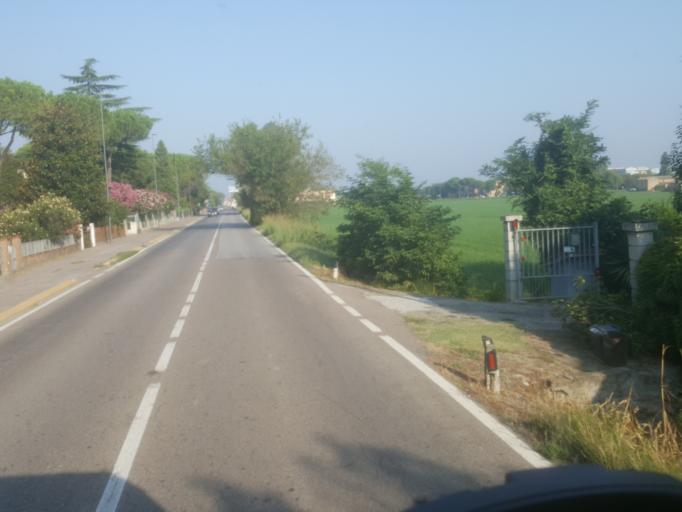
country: IT
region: Emilia-Romagna
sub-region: Provincia di Ravenna
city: Mezzano
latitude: 44.4623
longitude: 12.0945
